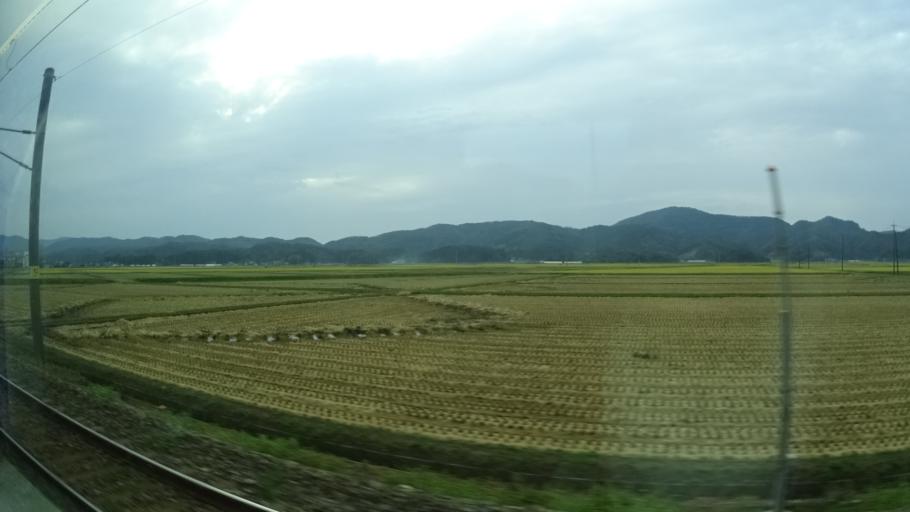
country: JP
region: Yamagata
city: Tsuruoka
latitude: 38.7215
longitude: 139.7411
